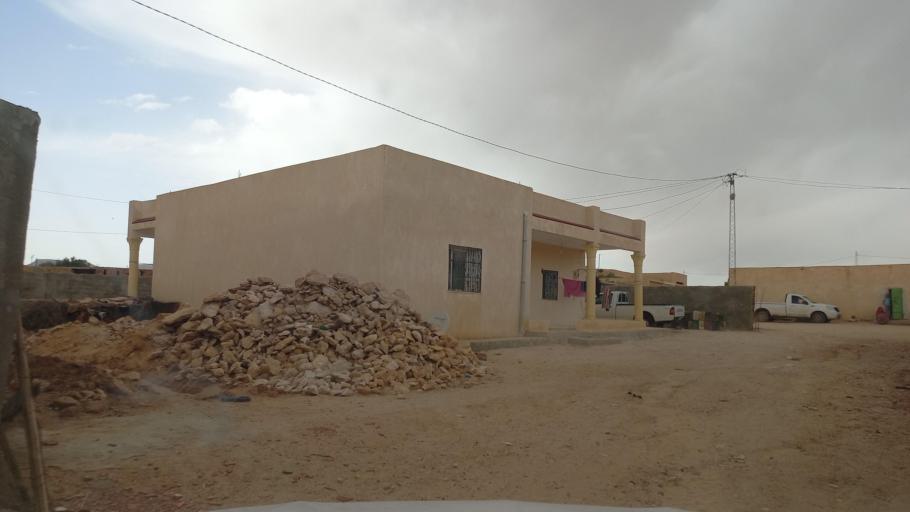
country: TN
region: Al Qasrayn
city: Sbiba
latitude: 35.3834
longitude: 9.0629
